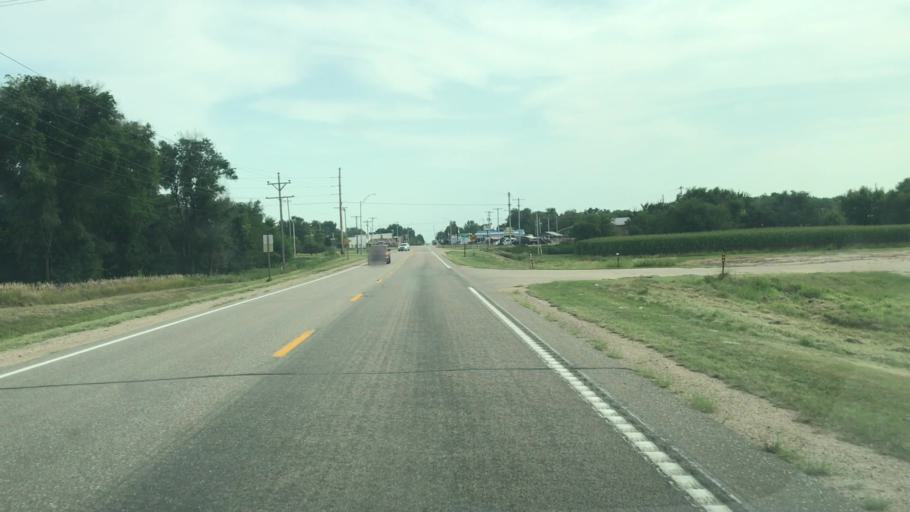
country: US
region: Nebraska
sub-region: Hall County
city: Wood River
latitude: 41.0055
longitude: -98.6075
